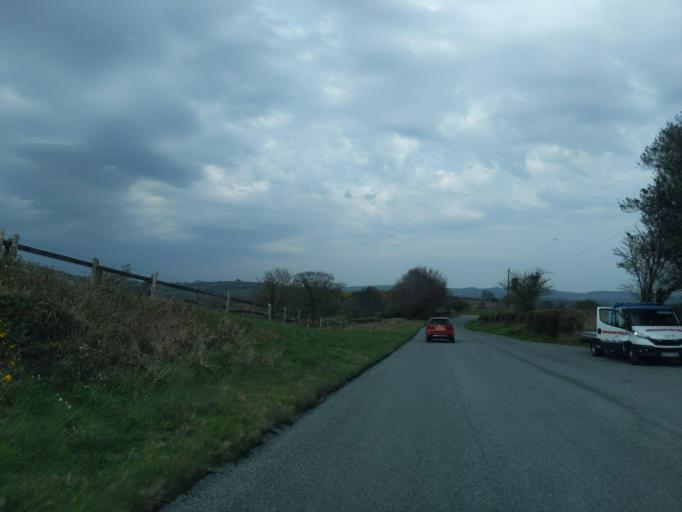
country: GB
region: England
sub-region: Devon
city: Ashburton
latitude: 50.6393
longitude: -3.8326
